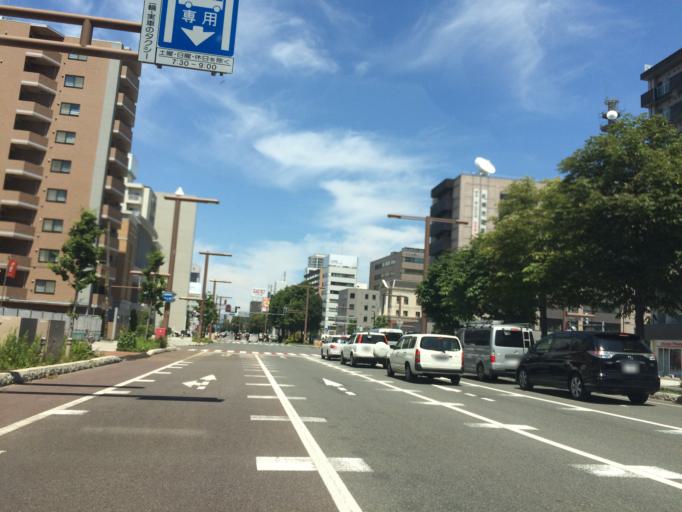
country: JP
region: Hokkaido
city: Sapporo
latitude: 43.0535
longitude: 141.3420
